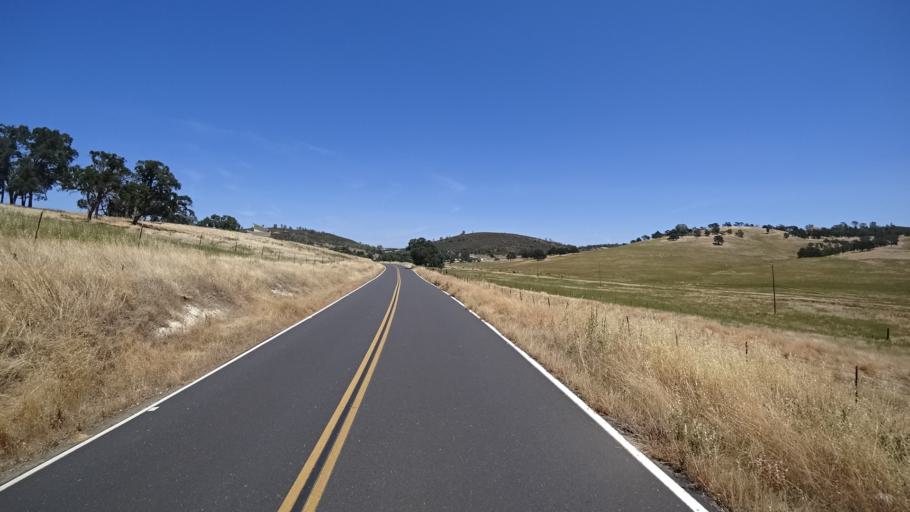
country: US
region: California
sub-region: Calaveras County
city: Valley Springs
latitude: 38.2295
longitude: -120.8172
